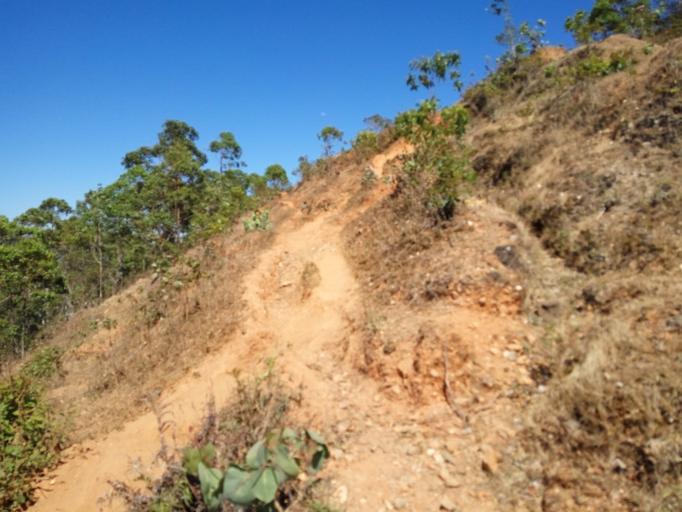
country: TL
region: Manatuto
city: Manatuto
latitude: -8.7395
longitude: 125.9041
